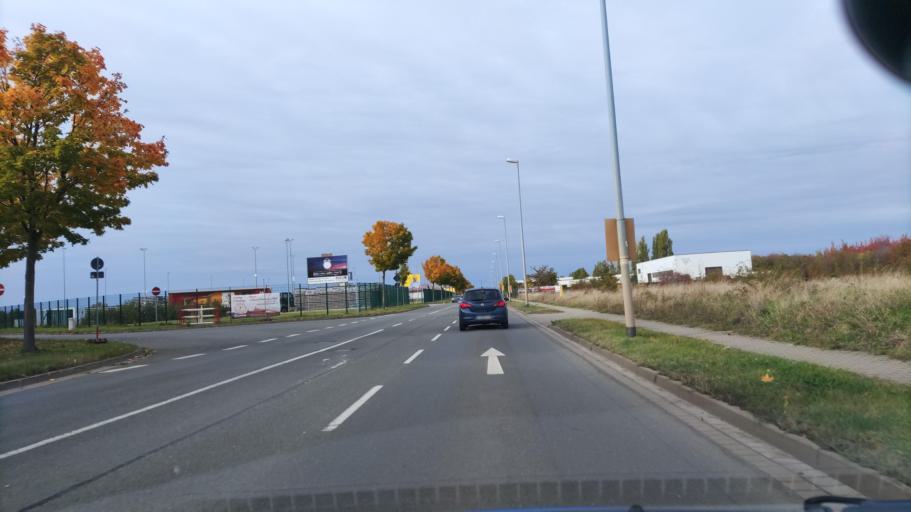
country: DE
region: Saxony-Anhalt
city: Wernigerode
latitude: 51.8447
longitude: 10.7577
